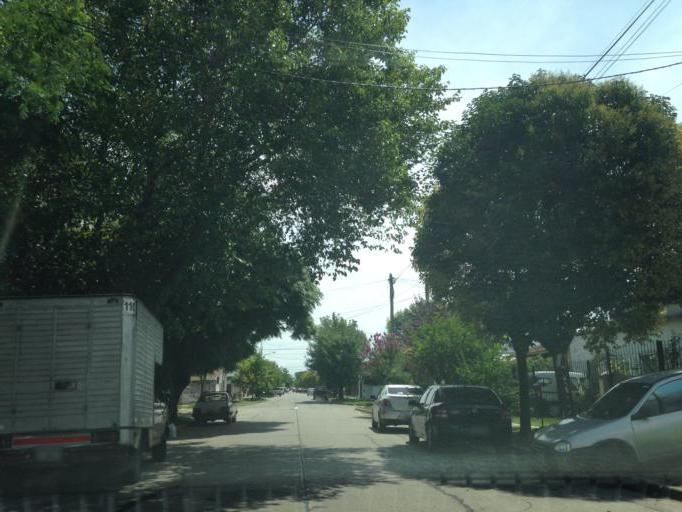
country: AR
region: Buenos Aires
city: Mar del Plata
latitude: -37.9775
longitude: -57.5609
